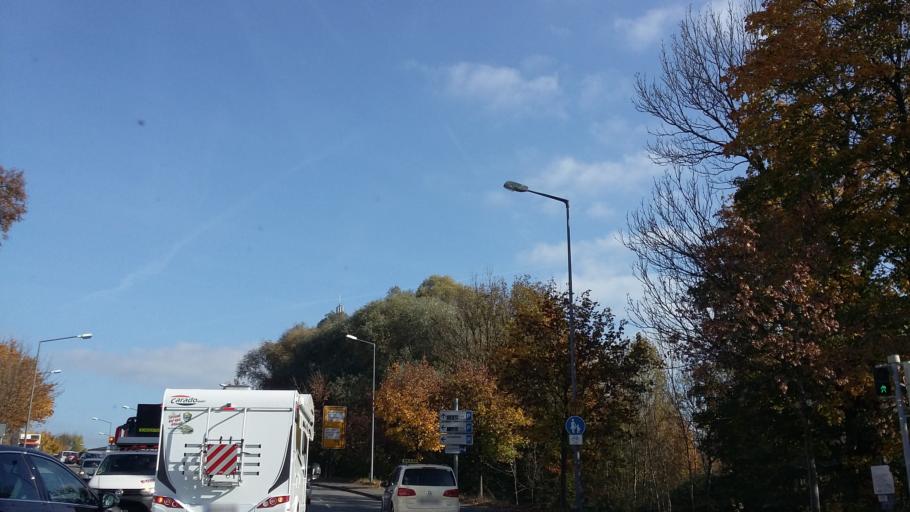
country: DE
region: Bavaria
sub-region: Upper Bavaria
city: Rosenheim
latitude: 47.8527
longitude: 12.1076
